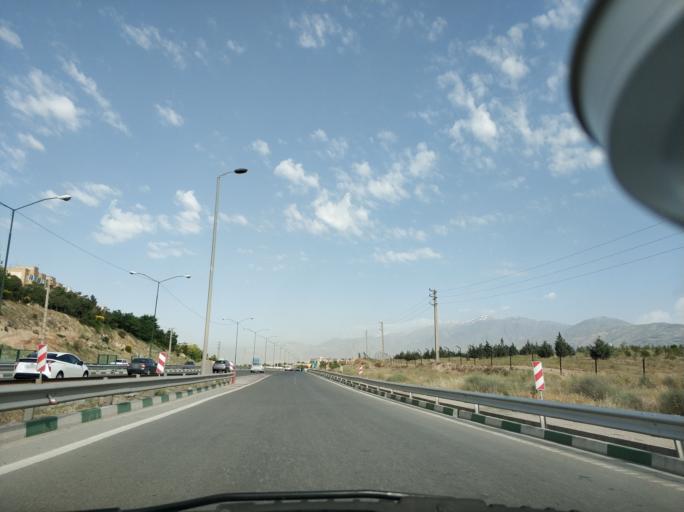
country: IR
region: Tehran
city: Tajrish
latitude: 35.7463
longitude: 51.5995
